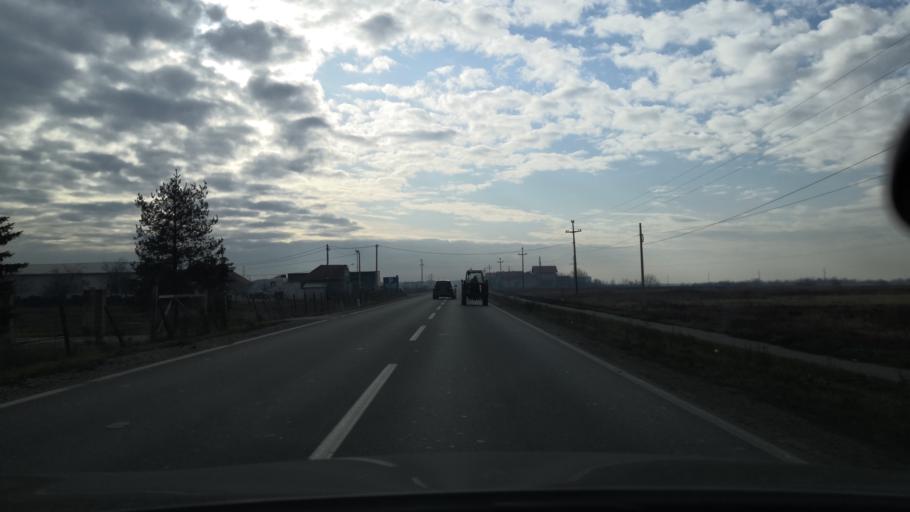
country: RS
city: Ugrinovci
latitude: 44.8644
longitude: 20.2044
